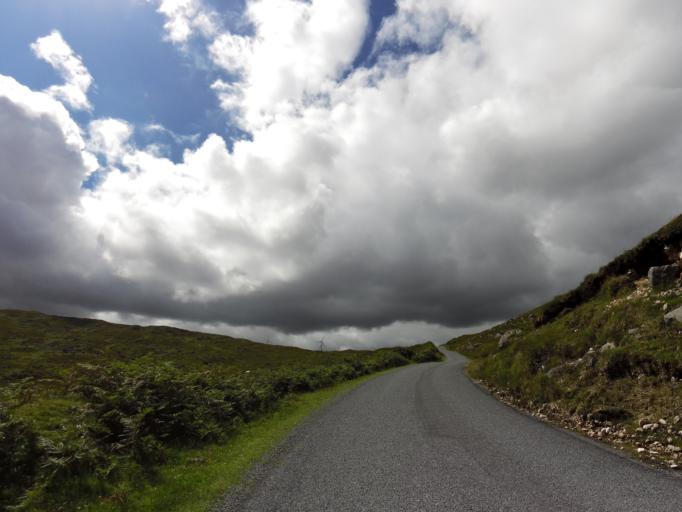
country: IE
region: Connaught
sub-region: County Galway
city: Oughterard
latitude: 53.3897
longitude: -9.3430
